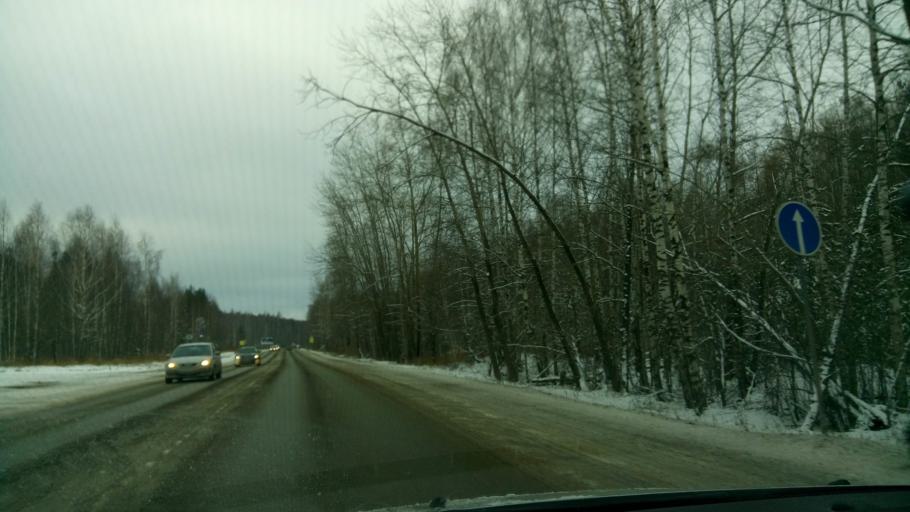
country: RU
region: Sverdlovsk
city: Polevskoy
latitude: 56.4675
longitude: 60.2261
